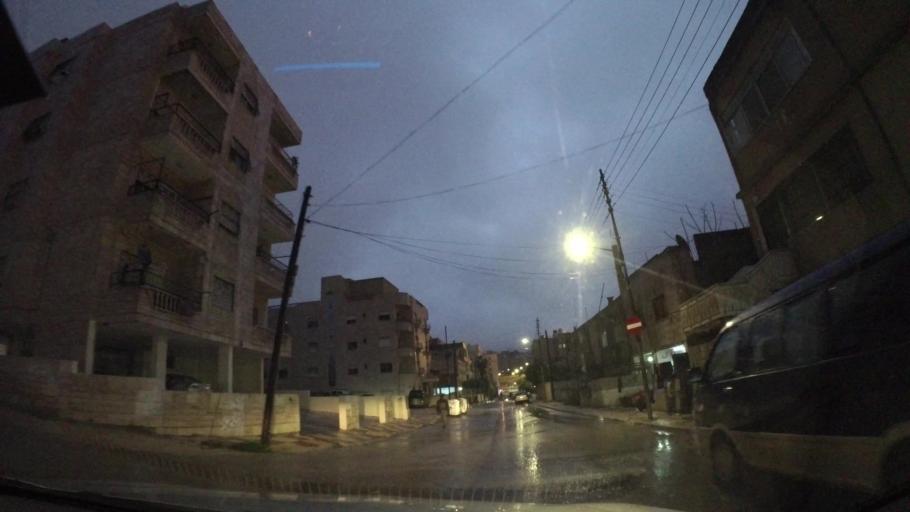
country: JO
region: Amman
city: Al Jubayhah
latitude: 32.0240
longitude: 35.8445
